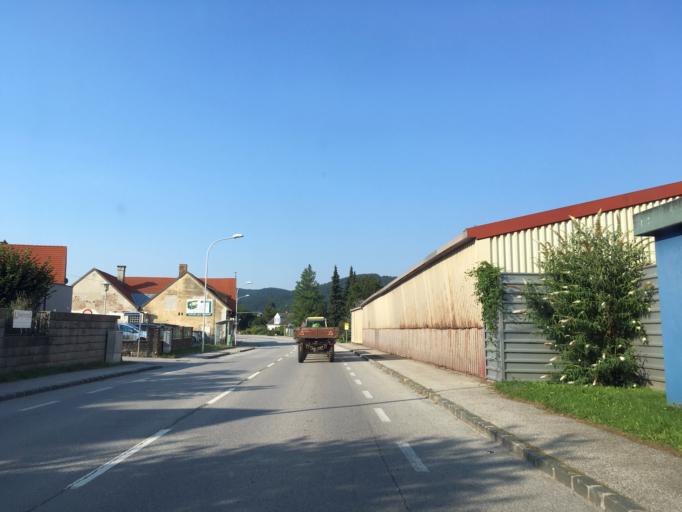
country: AT
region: Lower Austria
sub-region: Politischer Bezirk Neunkirchen
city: Warth
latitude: 47.6521
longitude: 16.1275
